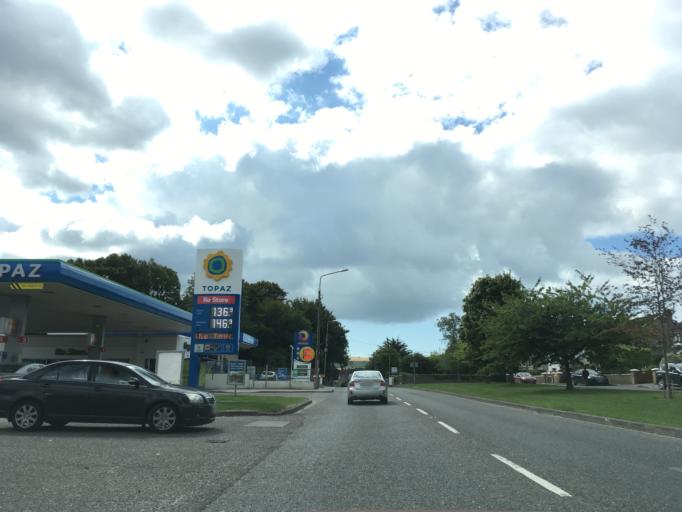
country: IE
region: Munster
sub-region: County Cork
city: Carrigaline
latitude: 51.8203
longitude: -8.3922
